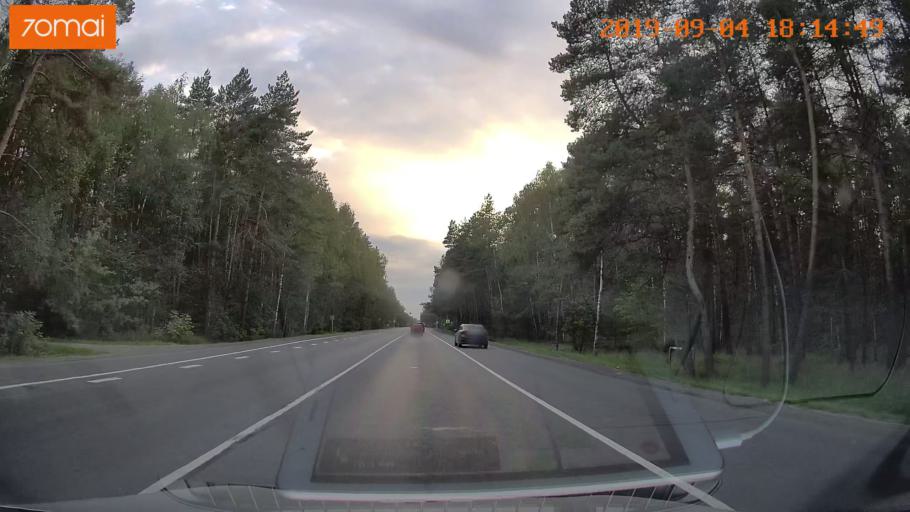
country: RU
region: Moskovskaya
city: Lopatinskiy
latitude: 55.3503
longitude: 38.7146
